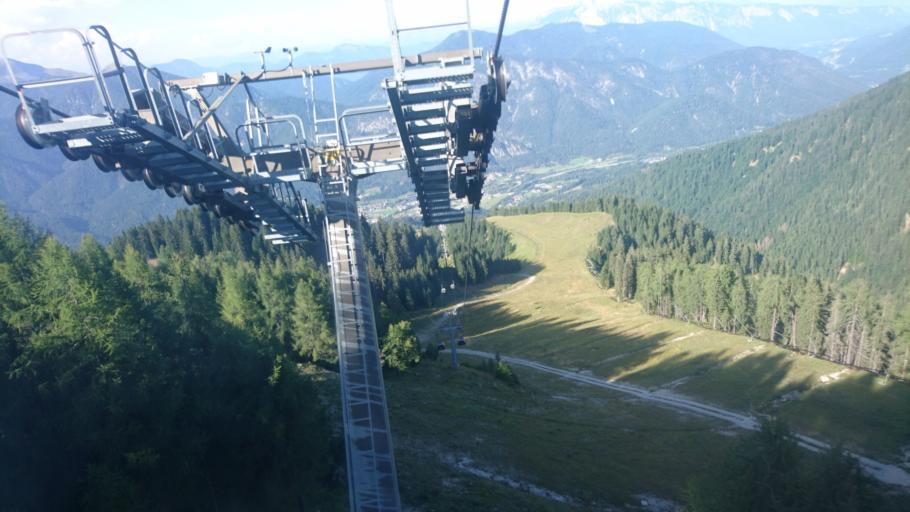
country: IT
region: Friuli Venezia Giulia
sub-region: Provincia di Udine
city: Tarvisio
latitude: 46.4826
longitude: 13.5213
